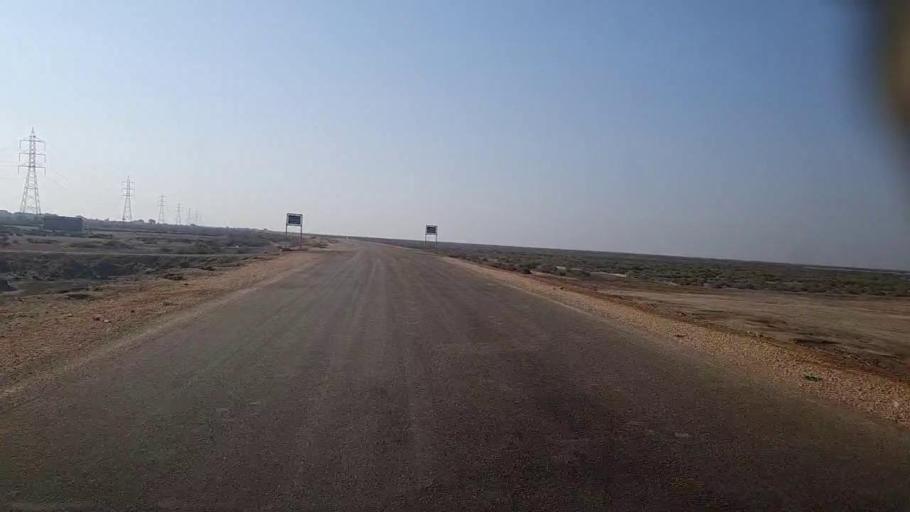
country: PK
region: Sindh
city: Gharo
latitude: 24.6287
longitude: 67.4971
